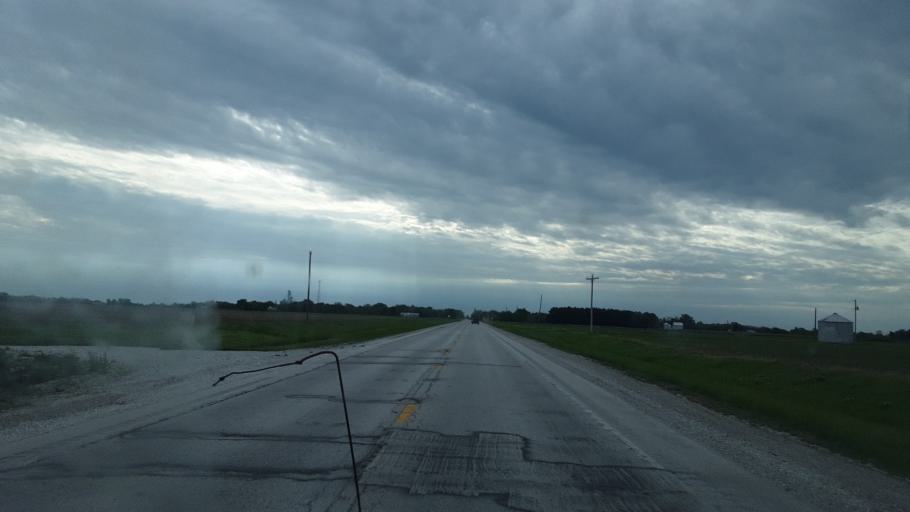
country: US
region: Illinois
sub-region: Hancock County
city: Hamilton
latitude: 40.3952
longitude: -91.2664
